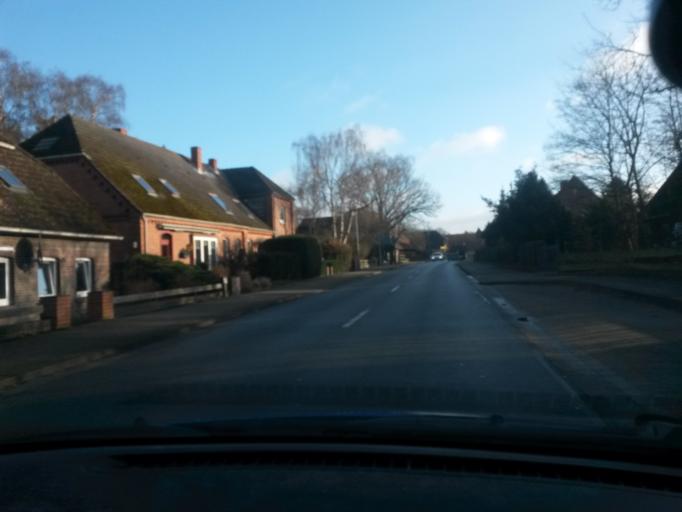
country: DE
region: Lower Saxony
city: Scharnebeck
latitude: 53.2904
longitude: 10.5010
